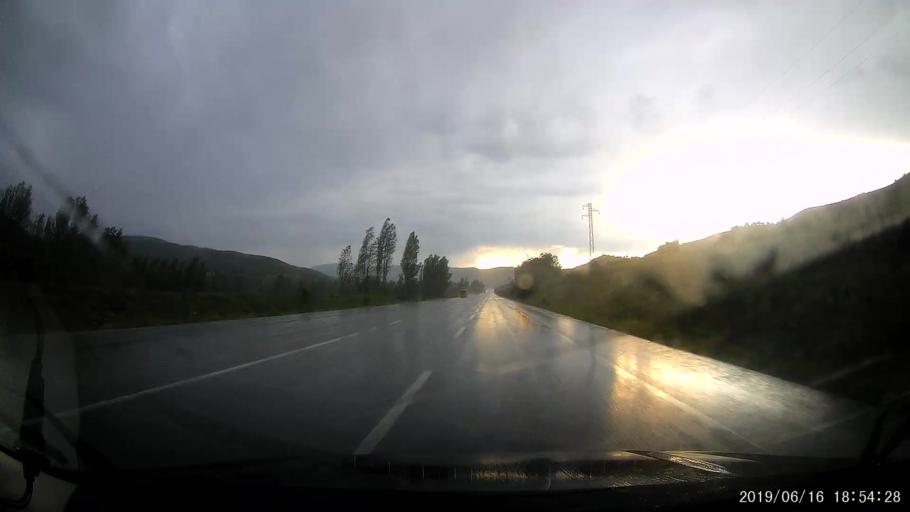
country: TR
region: Erzincan
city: Catalcam
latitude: 39.8970
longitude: 38.8529
